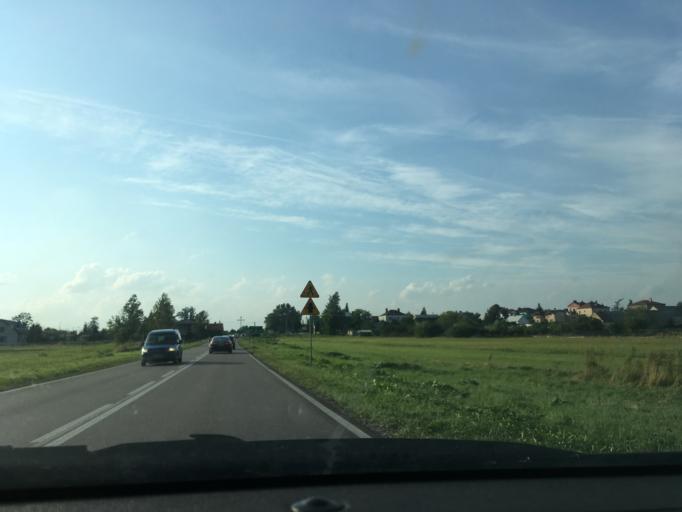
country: PL
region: Podlasie
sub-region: Powiat moniecki
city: Knyszyn
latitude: 53.3067
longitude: 22.9162
